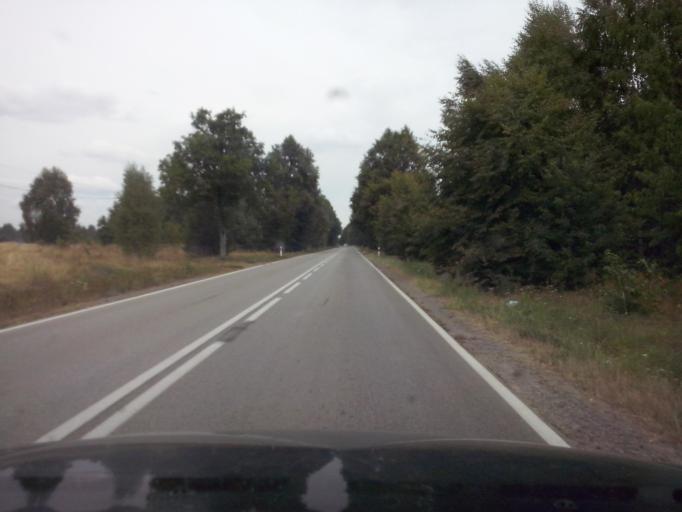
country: PL
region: Swietokrzyskie
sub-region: Powiat kielecki
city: Rakow
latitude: 50.6867
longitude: 21.0565
